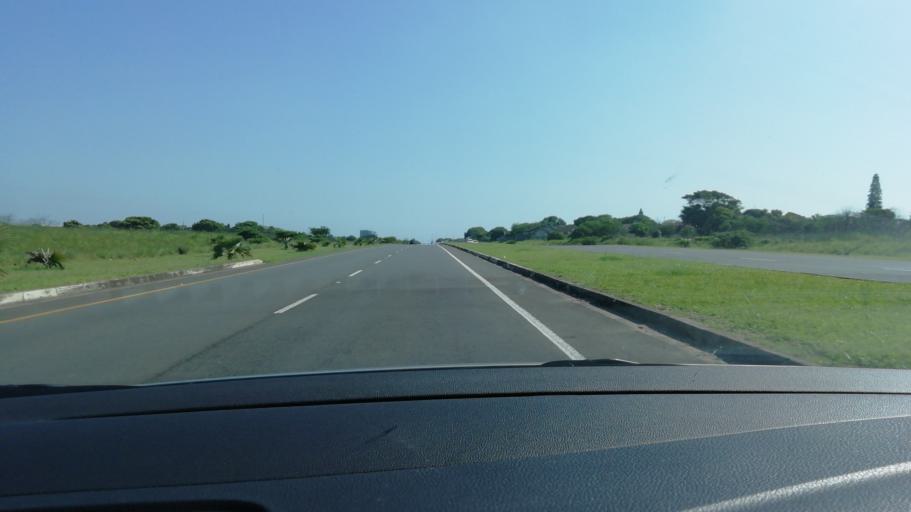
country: ZA
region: KwaZulu-Natal
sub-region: uThungulu District Municipality
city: Richards Bay
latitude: -28.7649
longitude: 32.0487
